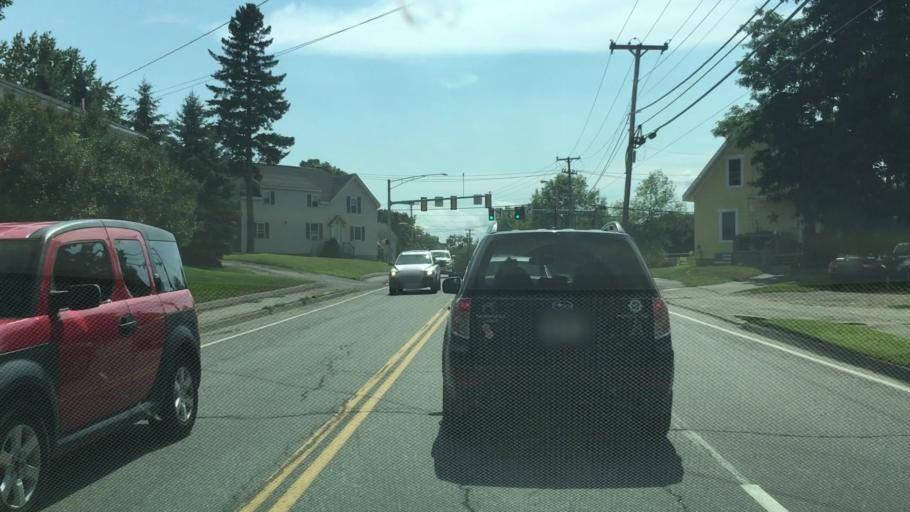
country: US
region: Maine
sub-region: Penobscot County
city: Bangor
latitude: 44.8138
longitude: -68.7675
